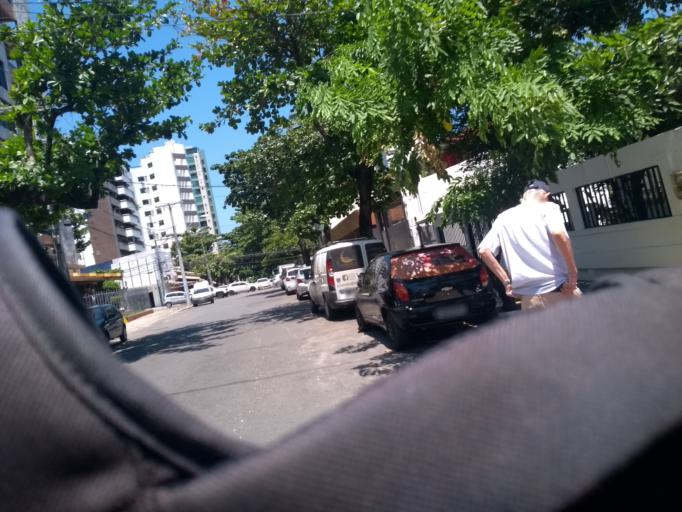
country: BR
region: Bahia
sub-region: Salvador
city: Salvador
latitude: -13.0006
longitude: -38.4568
